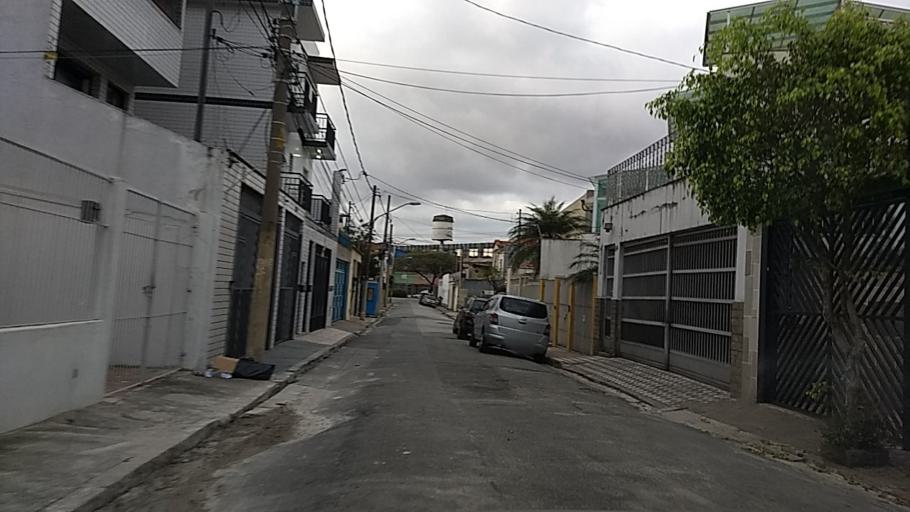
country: BR
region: Sao Paulo
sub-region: Sao Paulo
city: Sao Paulo
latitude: -23.5270
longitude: -46.6132
